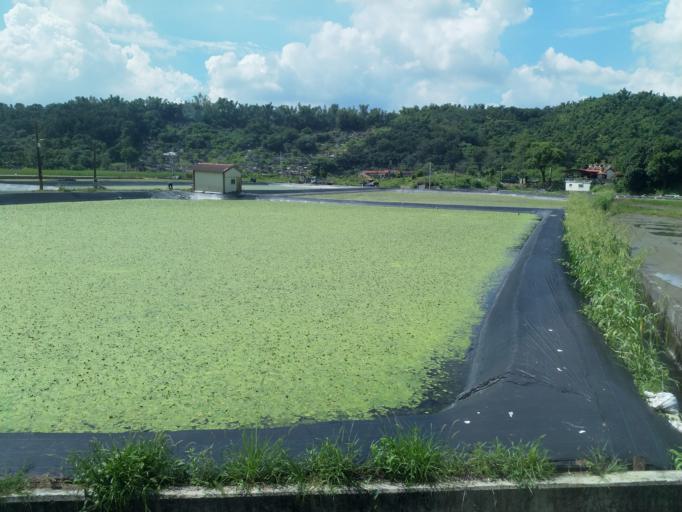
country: TW
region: Taiwan
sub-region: Pingtung
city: Pingtung
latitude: 22.8988
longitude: 120.5793
